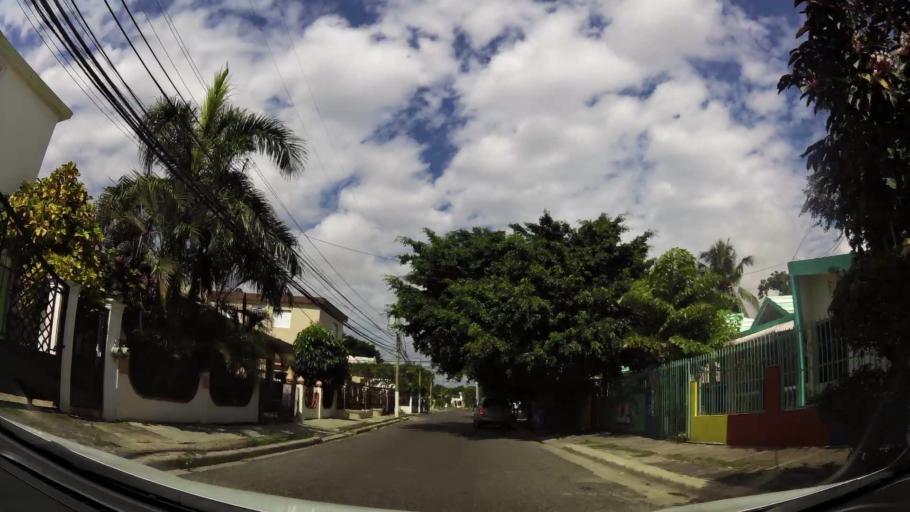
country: DO
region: Santiago
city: Santiago de los Caballeros
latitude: 19.4715
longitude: -70.6941
